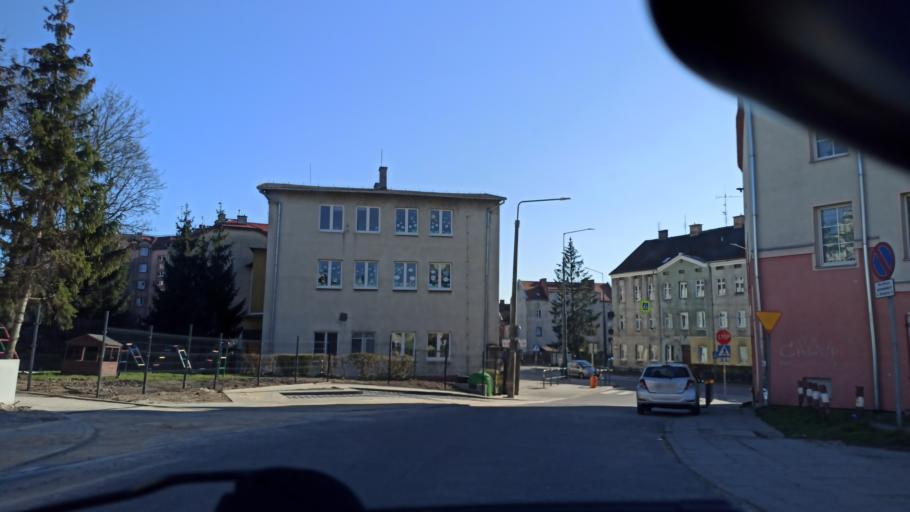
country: PL
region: Warmian-Masurian Voivodeship
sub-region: Powiat elblaski
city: Elblag
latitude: 54.1690
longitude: 19.3981
